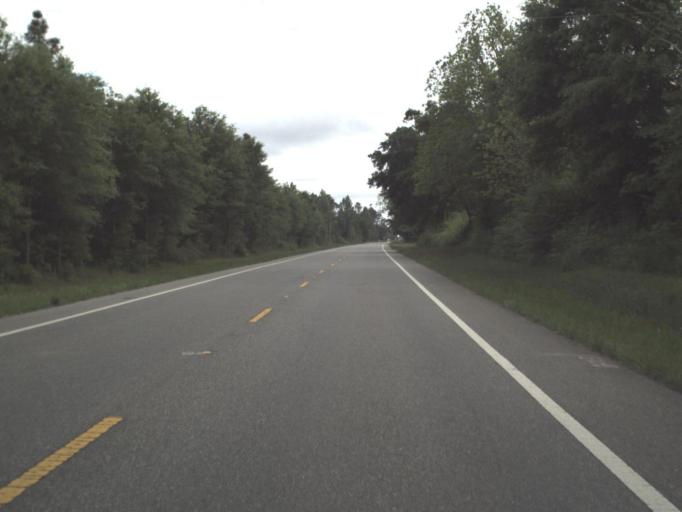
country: US
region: Florida
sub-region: Santa Rosa County
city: Point Baker
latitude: 30.7429
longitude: -87.0428
